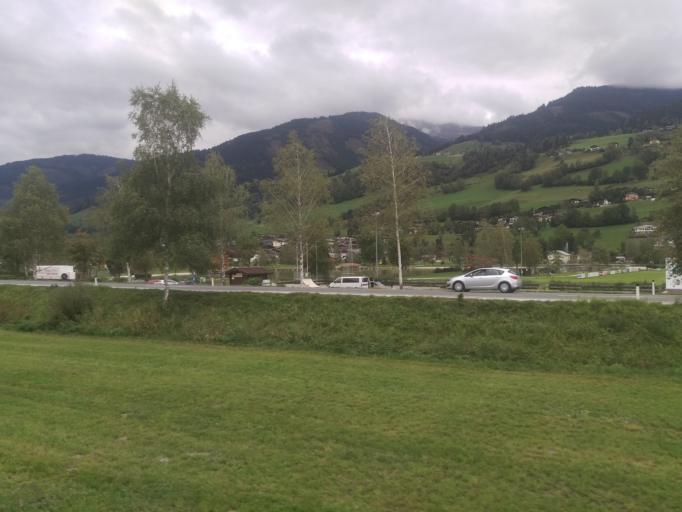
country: AT
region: Salzburg
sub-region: Politischer Bezirk Zell am See
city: Uttendorf
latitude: 47.2809
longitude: 12.5795
